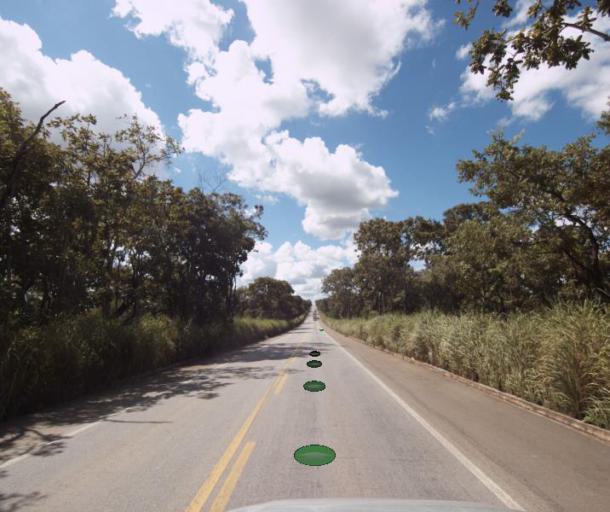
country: BR
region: Goias
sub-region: Porangatu
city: Porangatu
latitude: -13.6261
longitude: -49.0427
